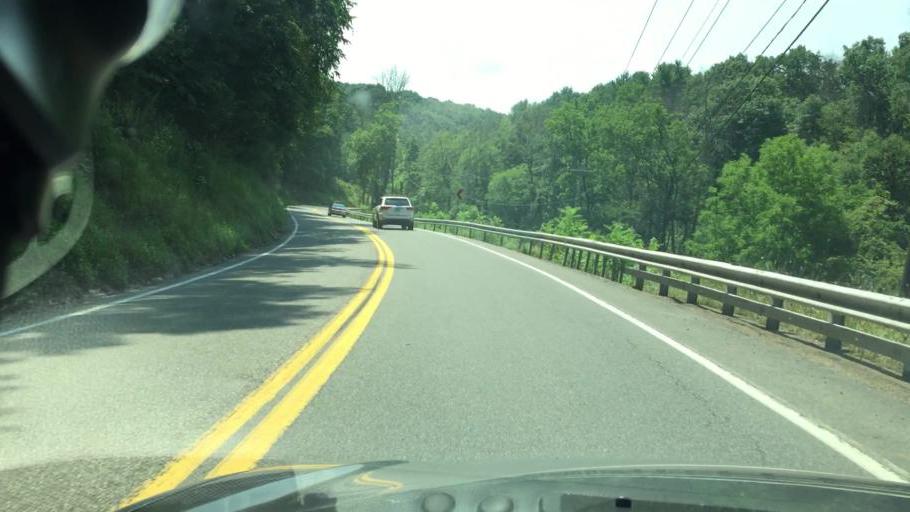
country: US
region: Pennsylvania
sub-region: Columbia County
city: Catawissa
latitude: 40.9165
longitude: -76.4736
